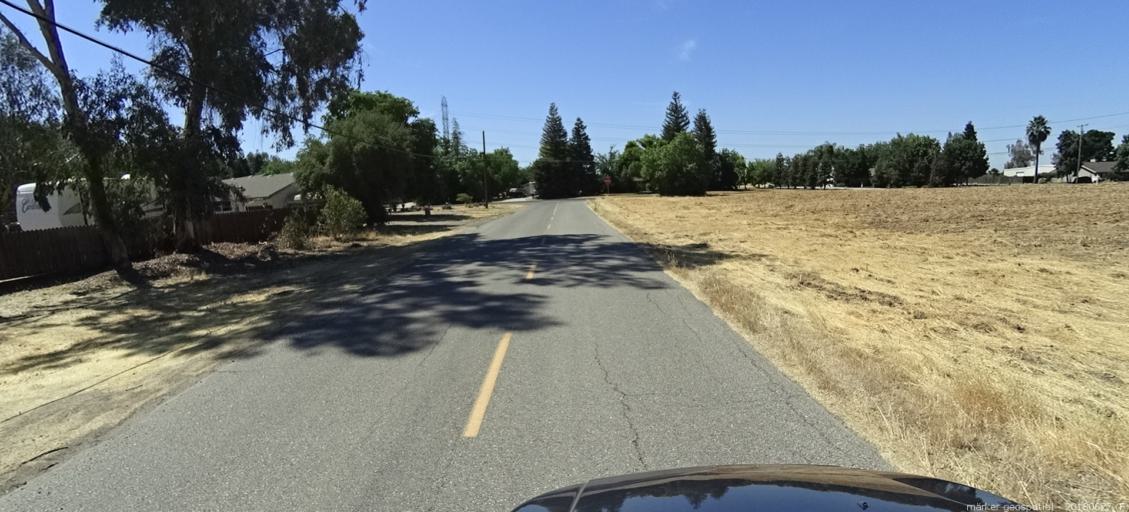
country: US
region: California
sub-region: Madera County
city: Bonadelle Ranchos-Madera Ranchos
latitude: 36.9204
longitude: -119.8753
